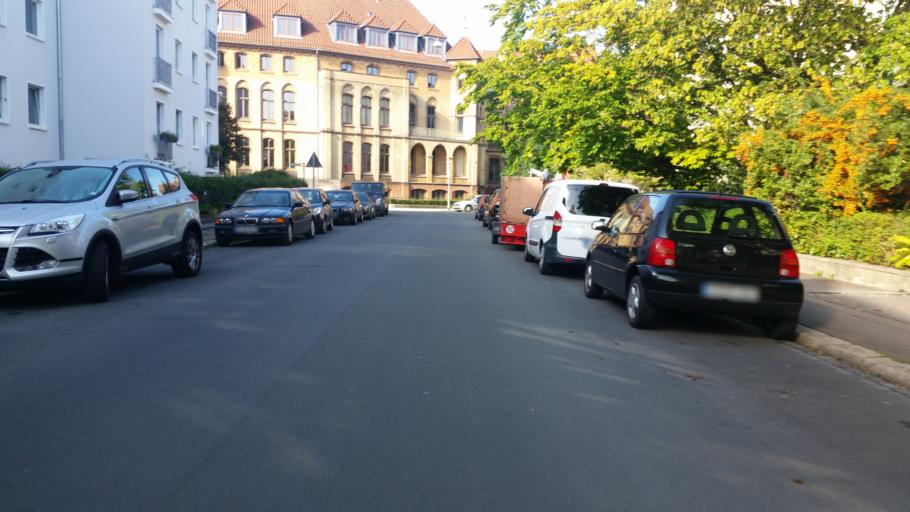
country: DE
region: Lower Saxony
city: Hannover
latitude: 52.3763
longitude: 9.7549
